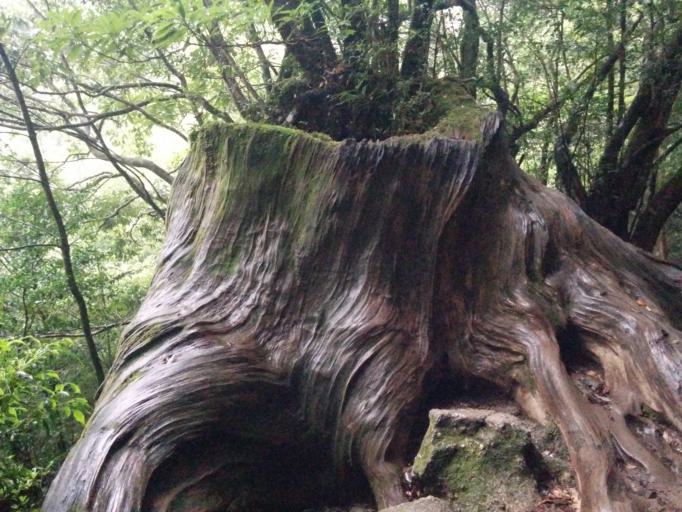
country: JP
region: Kagoshima
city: Nishinoomote
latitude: 30.3737
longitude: 130.5700
